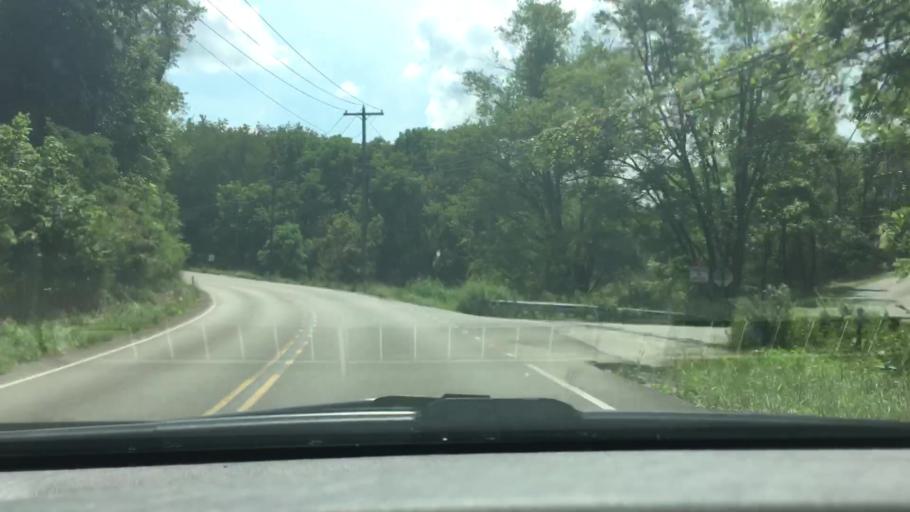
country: US
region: Pennsylvania
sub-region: Washington County
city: McMurray
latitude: 40.2425
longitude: -80.0966
